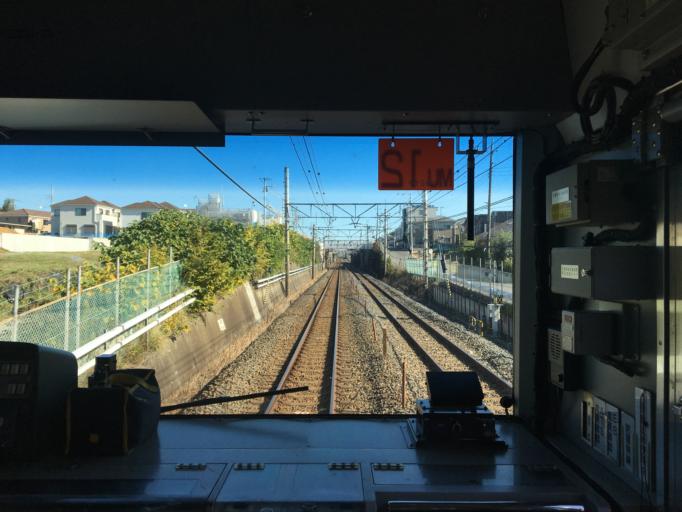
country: JP
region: Saitama
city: Shimotoda
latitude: 35.8555
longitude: 139.6831
